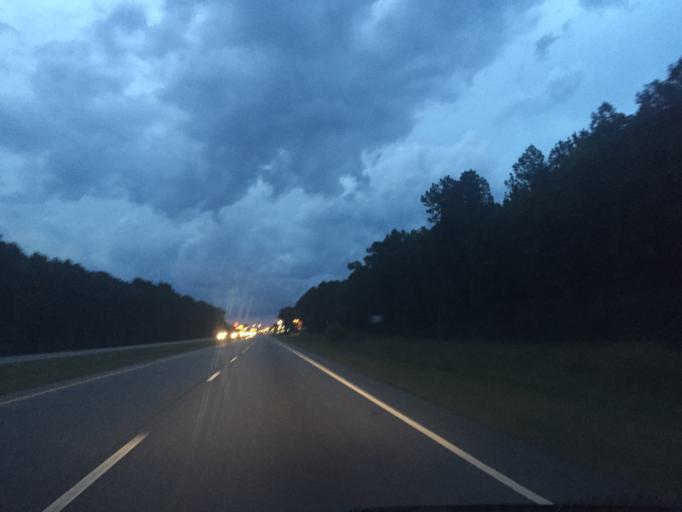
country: US
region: Georgia
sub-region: Bryan County
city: Richmond Hill
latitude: 31.9191
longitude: -81.3430
